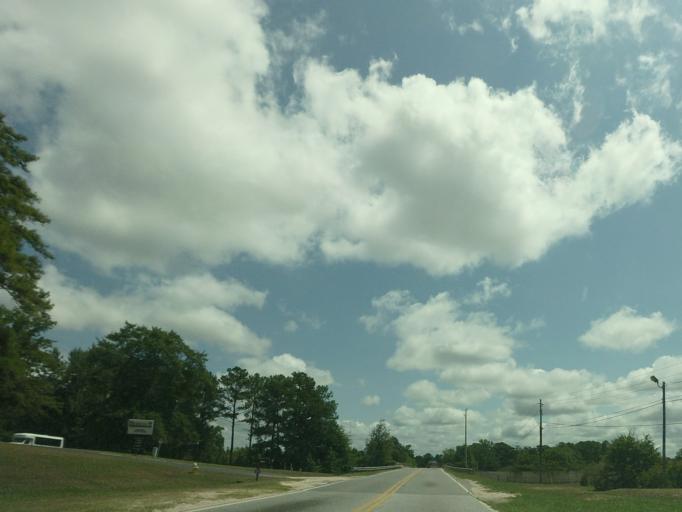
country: US
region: Georgia
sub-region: Bibb County
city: West Point
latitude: 32.8174
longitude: -83.7303
